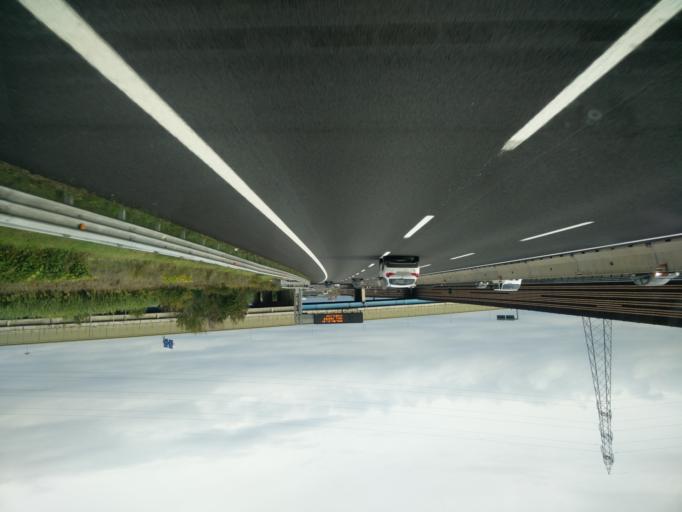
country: IT
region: Tuscany
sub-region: Province of Florence
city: Mantignano-Ugnano
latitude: 43.7713
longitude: 11.1637
